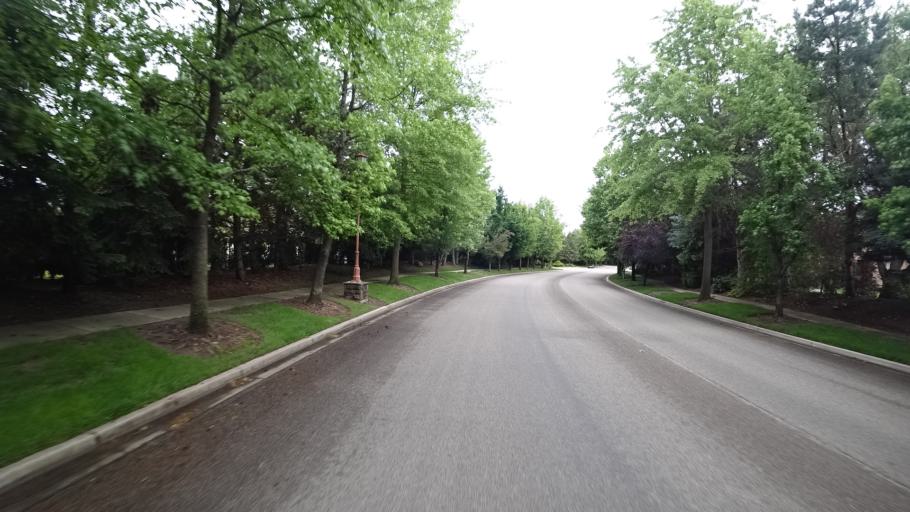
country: US
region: Idaho
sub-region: Ada County
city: Eagle
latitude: 43.6831
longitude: -116.3589
